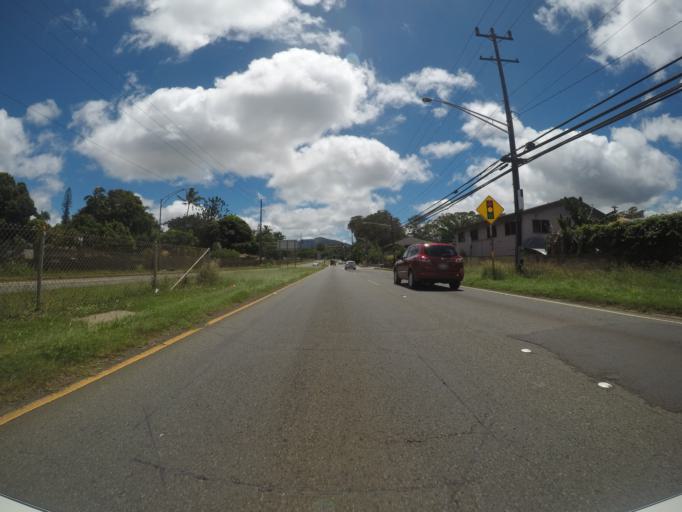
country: US
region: Hawaii
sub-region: Honolulu County
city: Wahiawa
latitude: 21.4897
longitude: -158.0346
